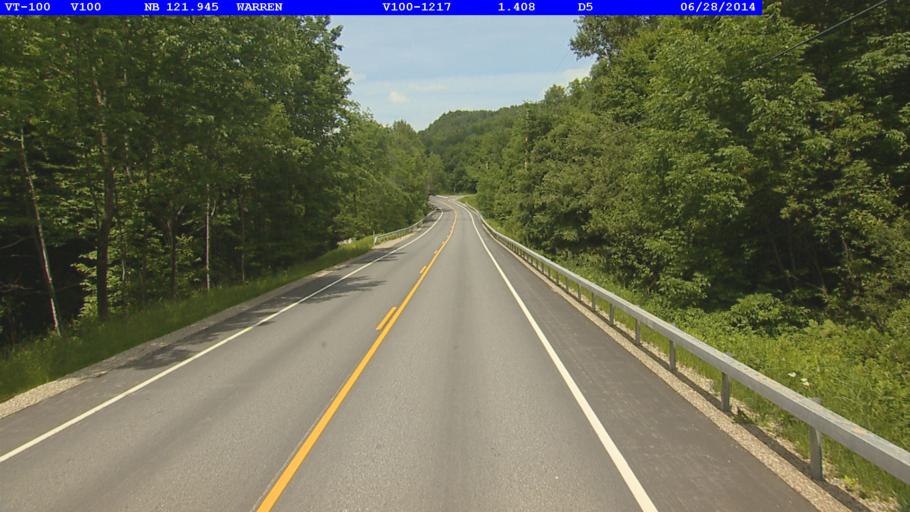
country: US
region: Vermont
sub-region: Washington County
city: Northfield
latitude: 44.0797
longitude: -72.8590
